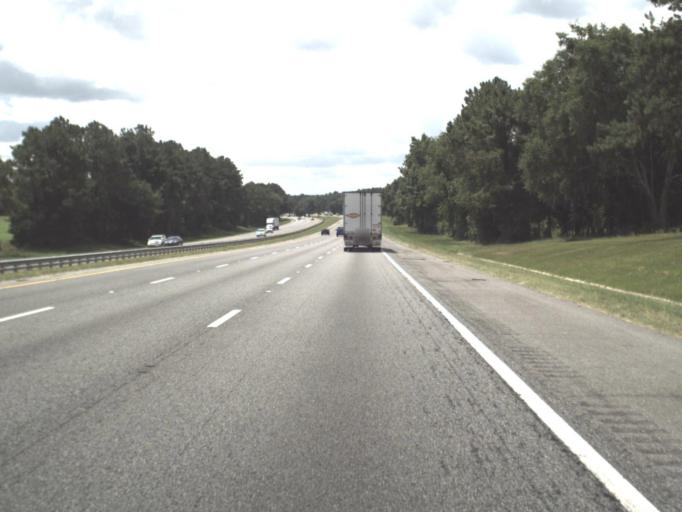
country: US
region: Florida
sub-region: Suwannee County
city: Wellborn
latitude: 30.2480
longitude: -82.7440
